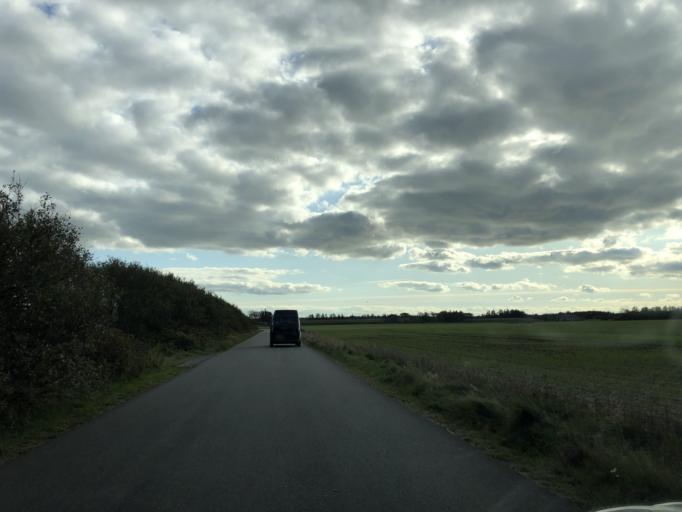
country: DK
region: Central Jutland
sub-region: Holstebro Kommune
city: Ulfborg
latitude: 56.3240
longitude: 8.1572
